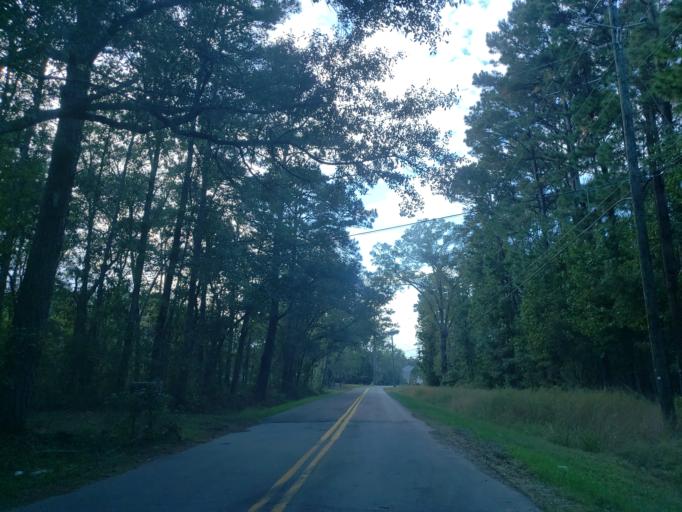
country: US
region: Georgia
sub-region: Chatham County
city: Georgetown
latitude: 31.9955
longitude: -81.2412
